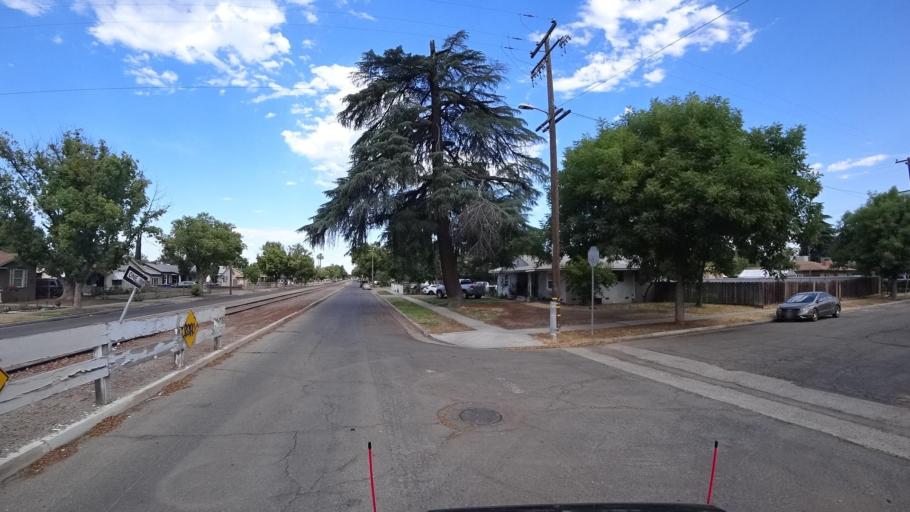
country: US
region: California
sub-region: Fresno County
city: Fresno
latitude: 36.7614
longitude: -119.7657
